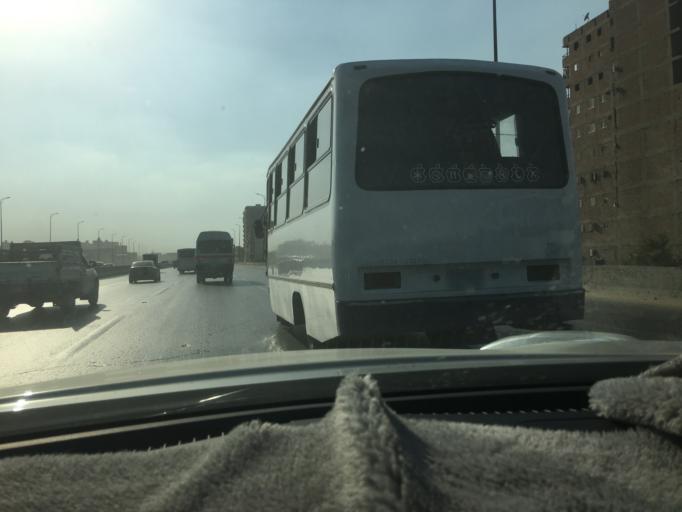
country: EG
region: Muhafazat al Qalyubiyah
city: Al Khankah
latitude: 30.1636
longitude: 31.3930
